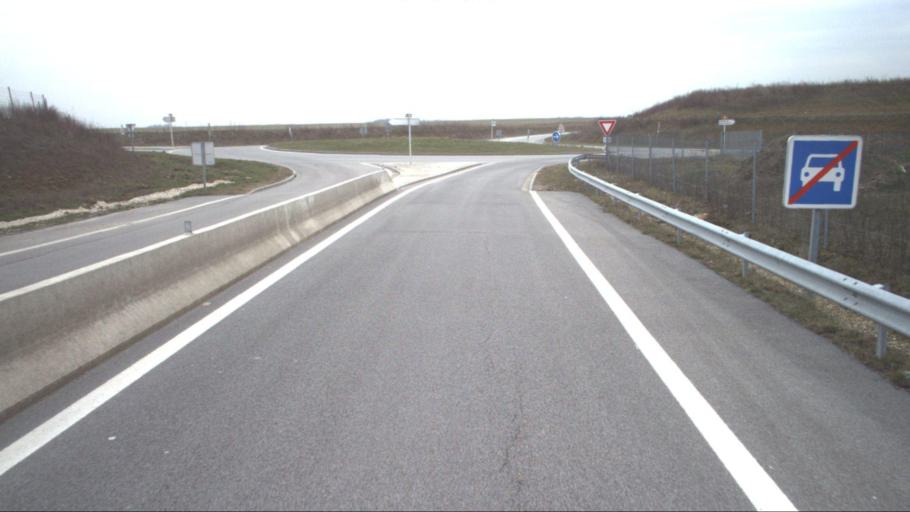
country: FR
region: Ile-de-France
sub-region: Departement des Yvelines
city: Sonchamp
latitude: 48.5802
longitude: 1.8337
